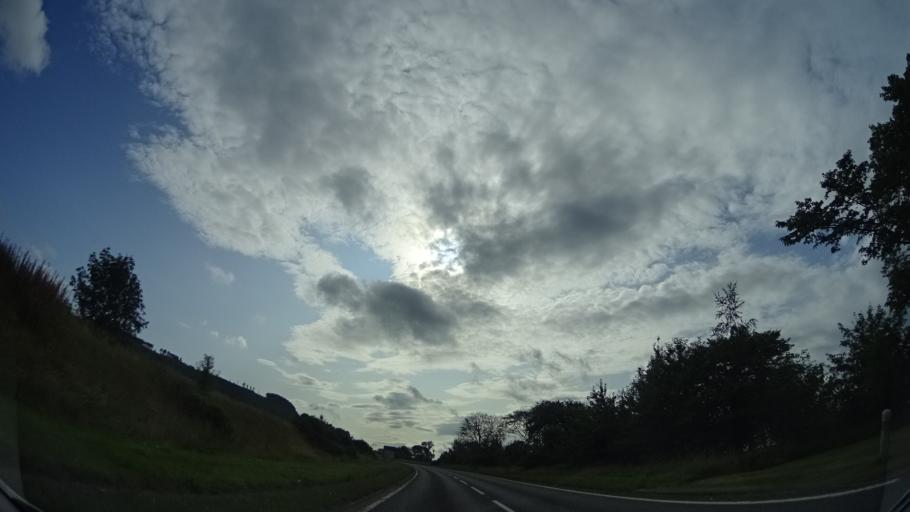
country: GB
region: Scotland
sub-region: Highland
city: Muir of Ord
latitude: 57.5583
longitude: -4.5445
